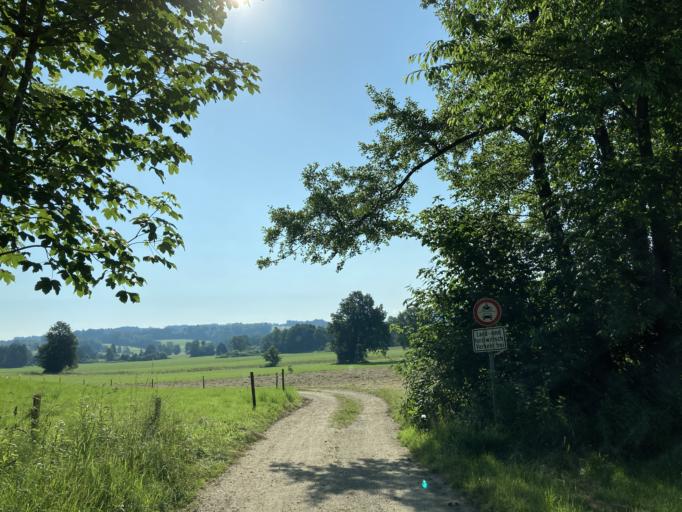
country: DE
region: Bavaria
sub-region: Upper Bavaria
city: Bad Endorf
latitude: 47.8959
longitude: 12.2738
